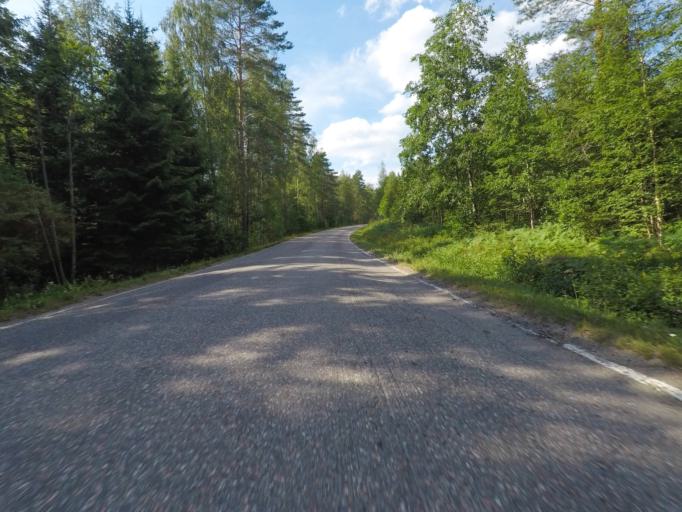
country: FI
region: Southern Savonia
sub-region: Mikkeli
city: Puumala
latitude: 61.6737
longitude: 28.2282
